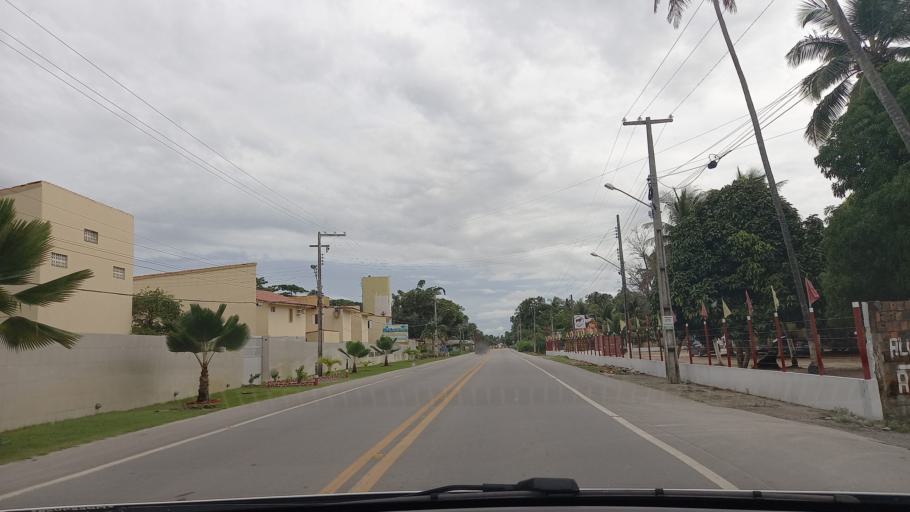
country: BR
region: Pernambuco
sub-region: Sao Jose Da Coroa Grande
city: Sao Jose da Coroa Grande
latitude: -8.9173
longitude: -35.1544
